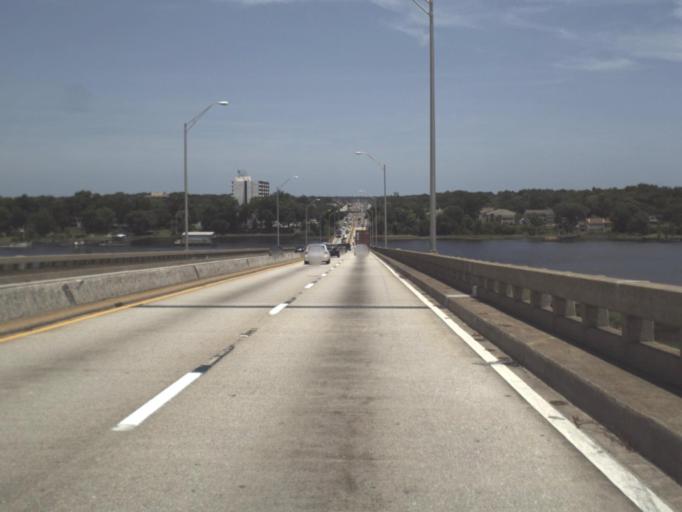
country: US
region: Florida
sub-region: Duval County
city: Jacksonville
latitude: 30.3272
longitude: -81.6178
